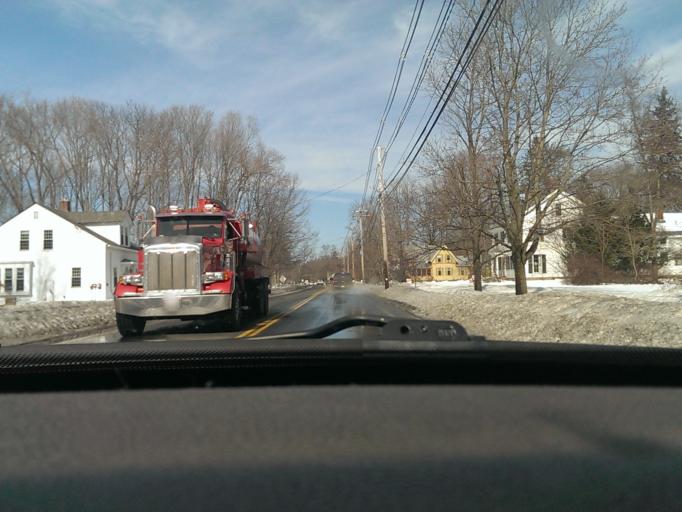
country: US
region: Massachusetts
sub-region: Hampden County
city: Wilbraham
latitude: 42.1158
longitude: -72.4333
